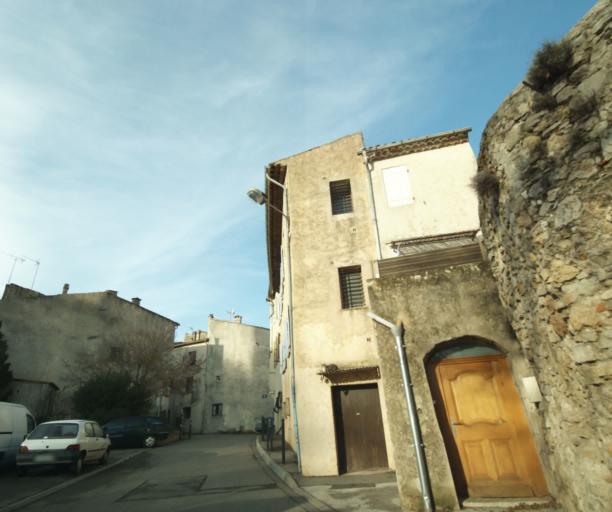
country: FR
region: Provence-Alpes-Cote d'Azur
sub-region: Departement du Var
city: Tourves
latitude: 43.4071
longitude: 5.9227
